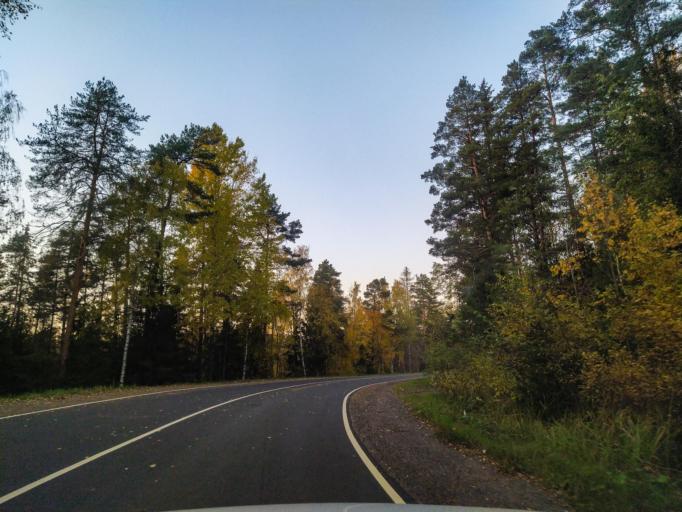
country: RU
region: Leningrad
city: Kuznechnoye
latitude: 61.1043
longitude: 29.9623
